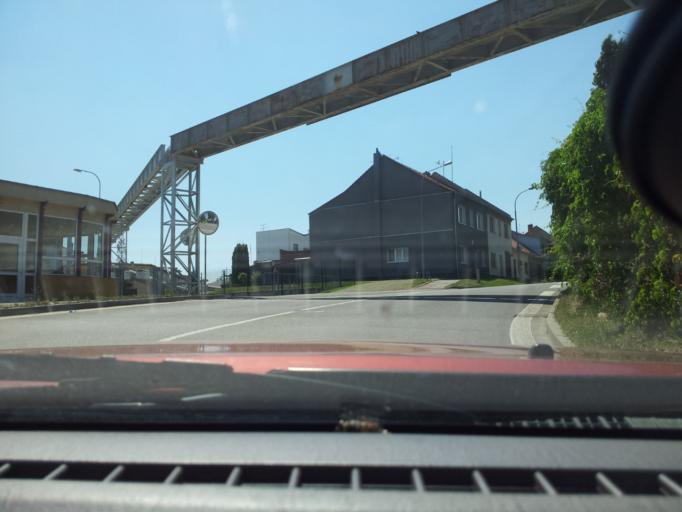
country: CZ
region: South Moravian
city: Moravany
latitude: 49.1634
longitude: 16.6060
